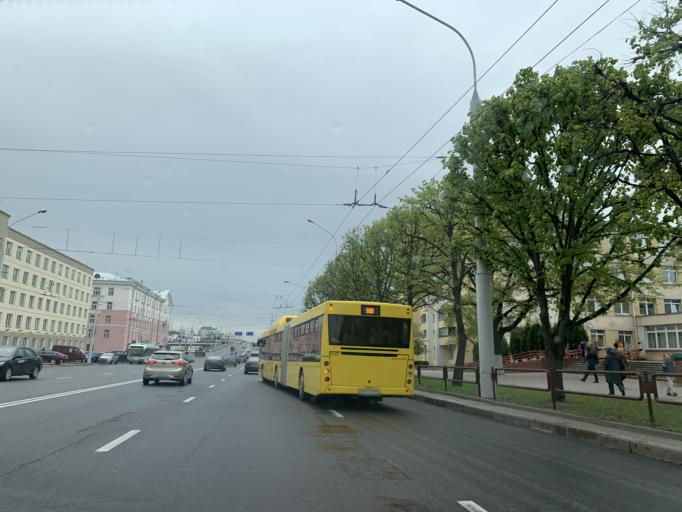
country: BY
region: Minsk
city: Minsk
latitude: 53.8803
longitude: 27.5356
